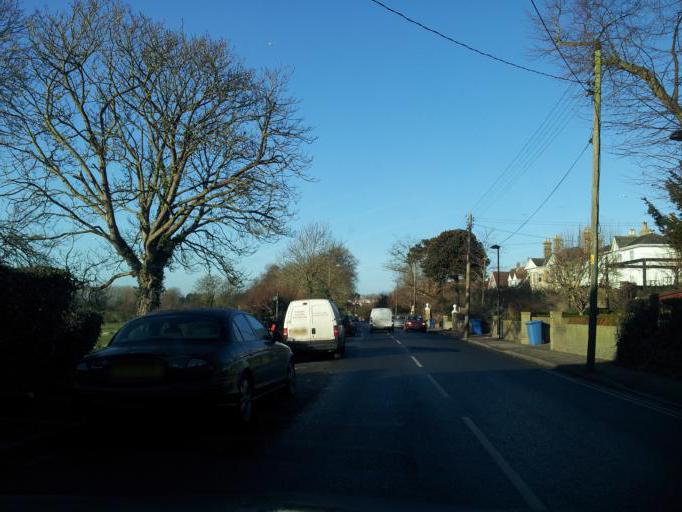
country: GB
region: England
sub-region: Suffolk
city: Sudbury
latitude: 52.0464
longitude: 0.7264
